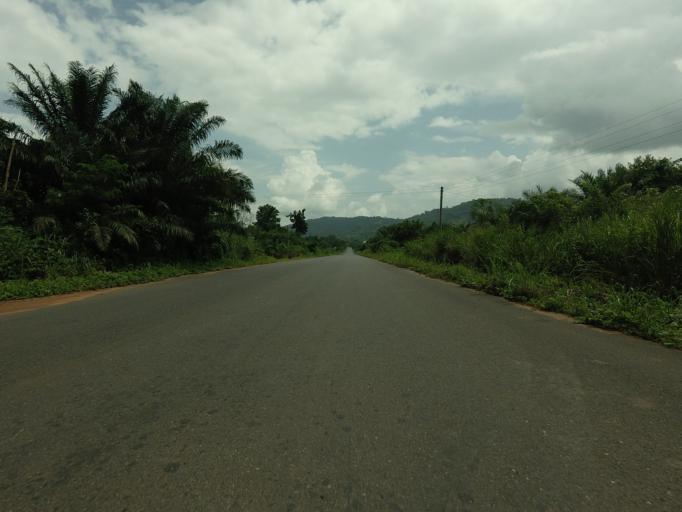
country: GH
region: Volta
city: Ho
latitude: 6.5418
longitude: 0.2450
